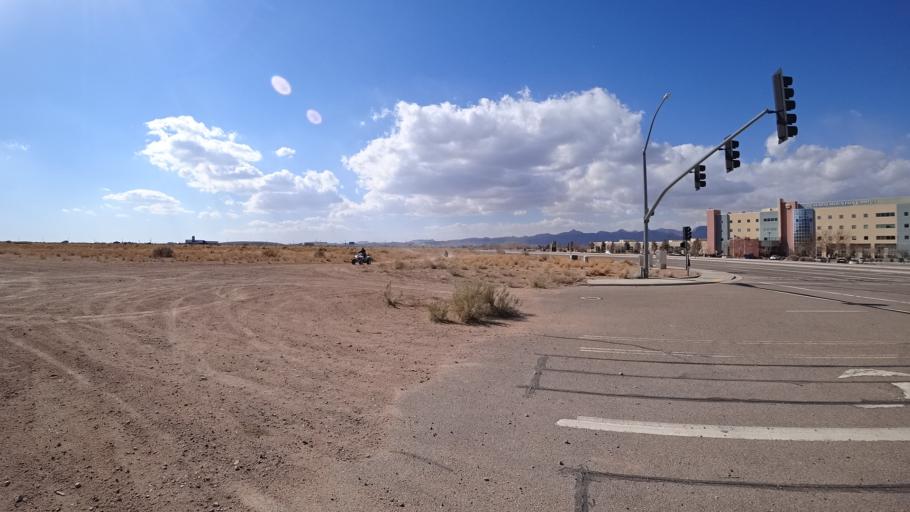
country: US
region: Arizona
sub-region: Mohave County
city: New Kingman-Butler
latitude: 35.2177
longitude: -113.9839
